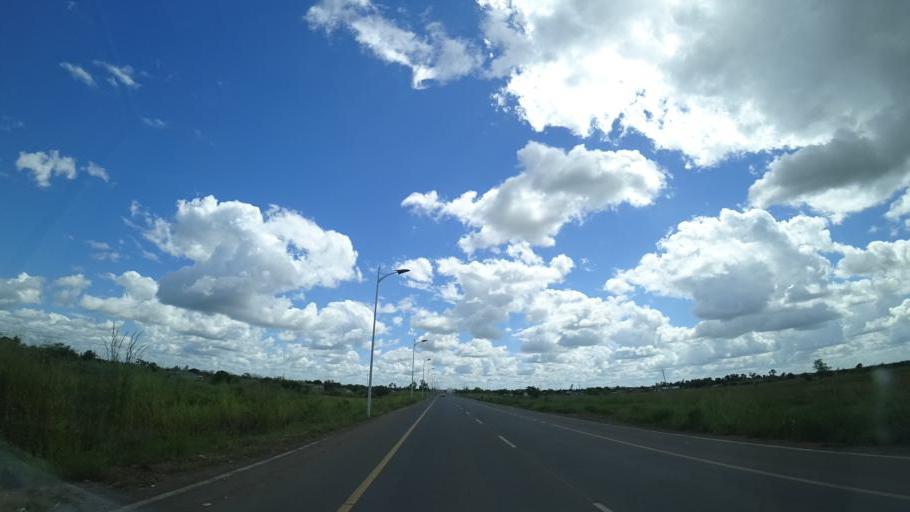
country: MZ
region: Sofala
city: Dondo
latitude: -19.2808
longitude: 34.2206
